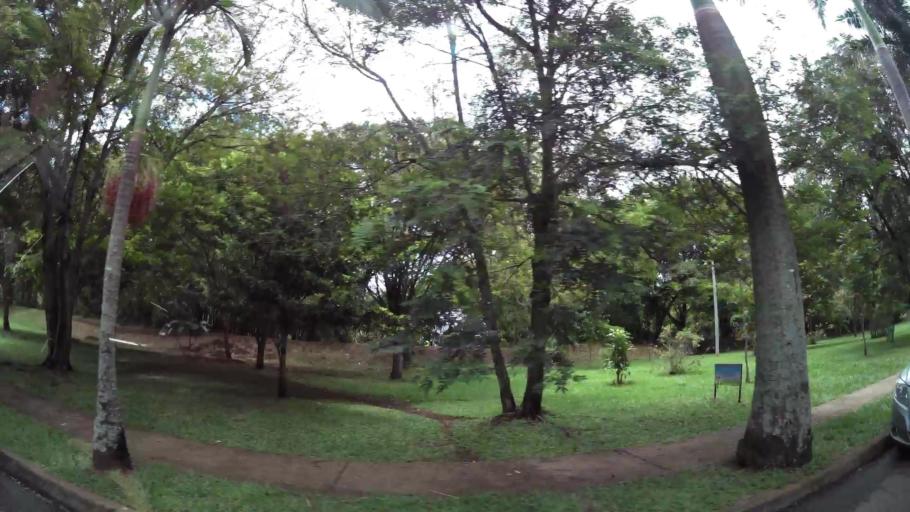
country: CO
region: Valle del Cauca
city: Cali
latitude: 3.3855
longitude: -76.5347
